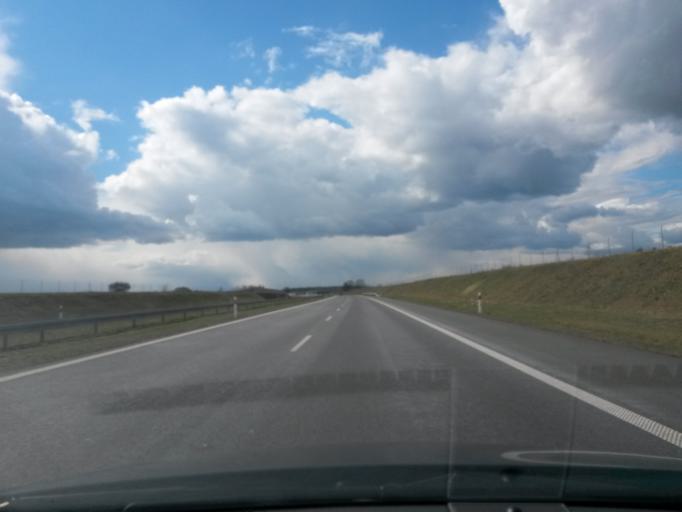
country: PL
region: Greater Poland Voivodeship
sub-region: Powiat turecki
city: Wladyslawow
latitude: 52.1512
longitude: 18.4863
